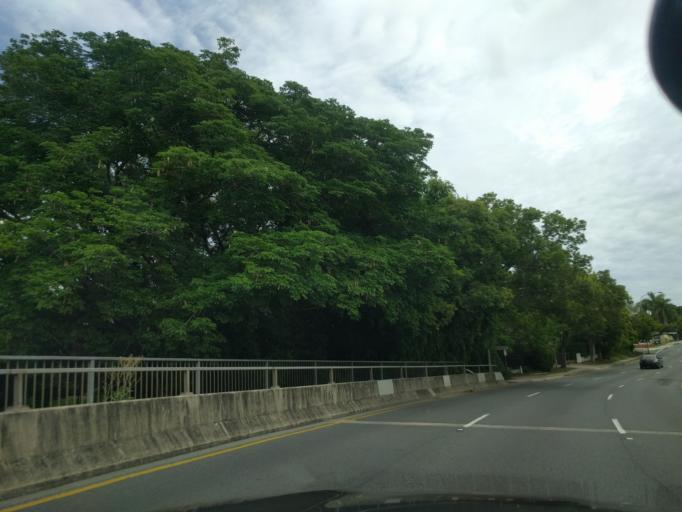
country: AU
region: Queensland
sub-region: Brisbane
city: Wilston
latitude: -27.4429
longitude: 153.0070
